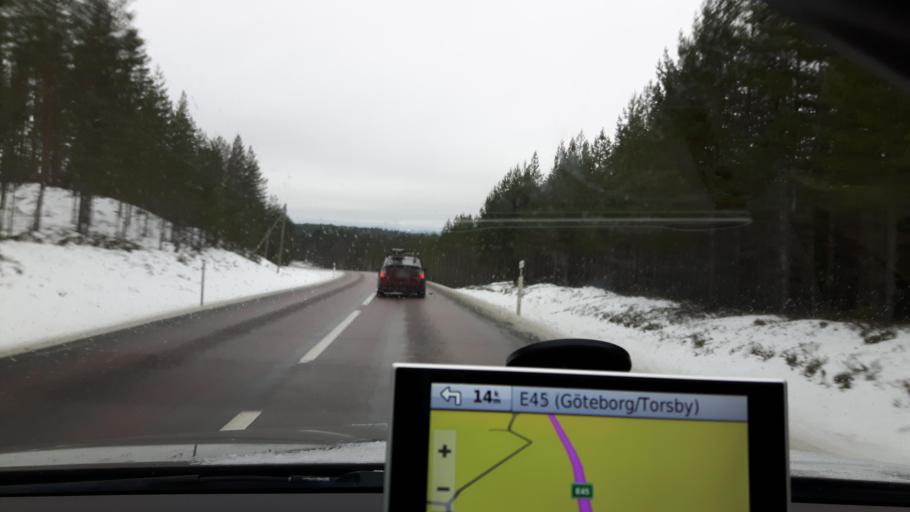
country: SE
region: Vaermland
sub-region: Torsby Kommun
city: Torsby
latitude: 60.3734
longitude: 13.2097
